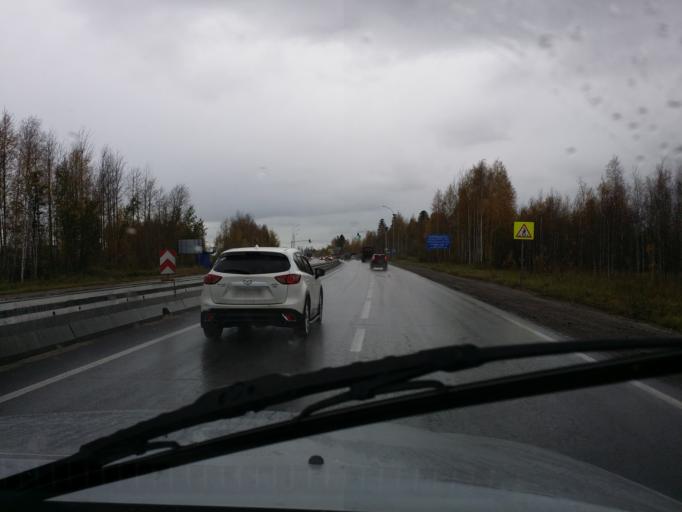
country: RU
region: Khanty-Mansiyskiy Avtonomnyy Okrug
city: Megion
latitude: 61.0641
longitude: 76.1897
